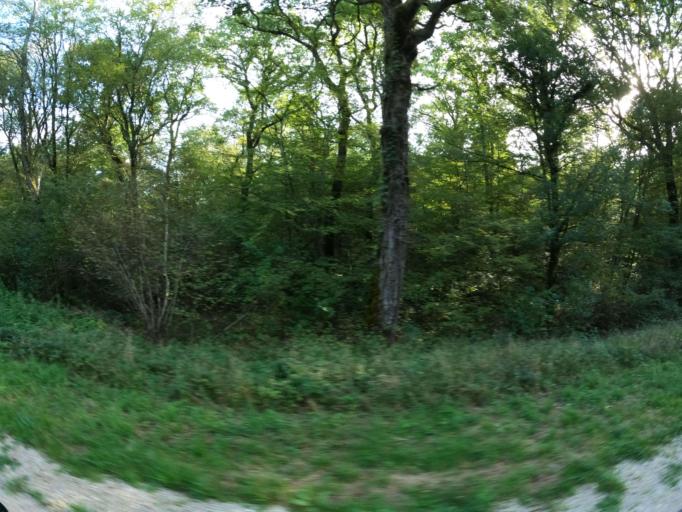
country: FR
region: Franche-Comte
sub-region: Departement du Jura
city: Montmorot
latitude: 46.7213
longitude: 5.5152
